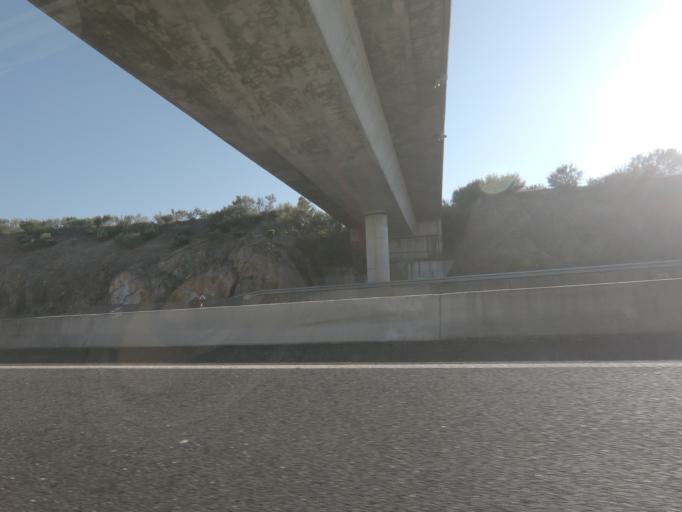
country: ES
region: Galicia
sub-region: Provincia de Ourense
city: Oimbra
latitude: 41.8177
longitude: -7.4167
